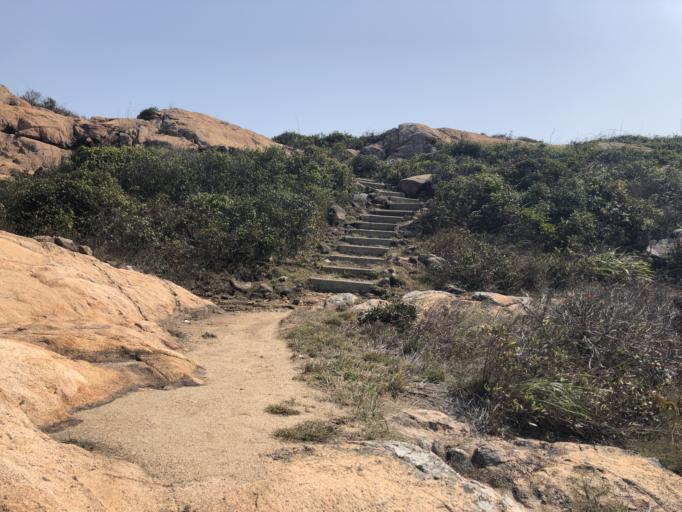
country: HK
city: Sok Kwu Wan
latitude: 22.1693
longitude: 114.2570
